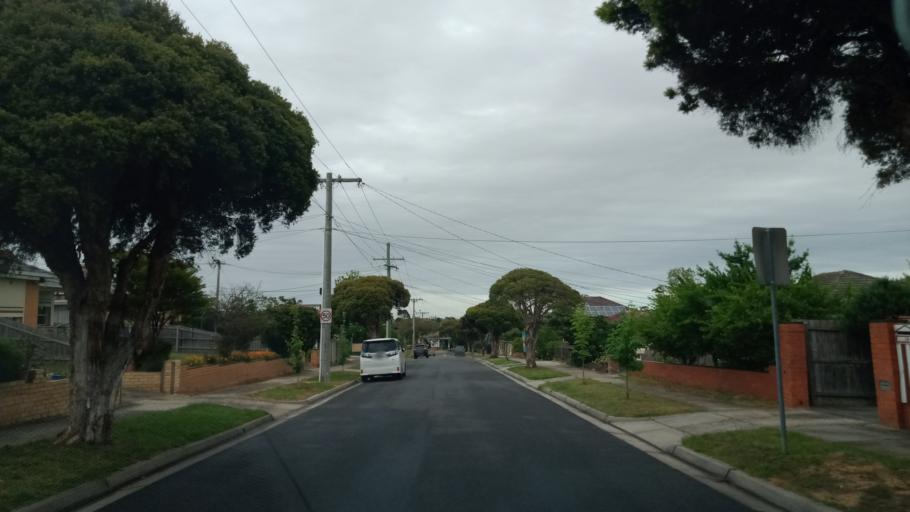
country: AU
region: Victoria
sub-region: Greater Dandenong
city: Springvale
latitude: -37.9412
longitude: 145.1591
